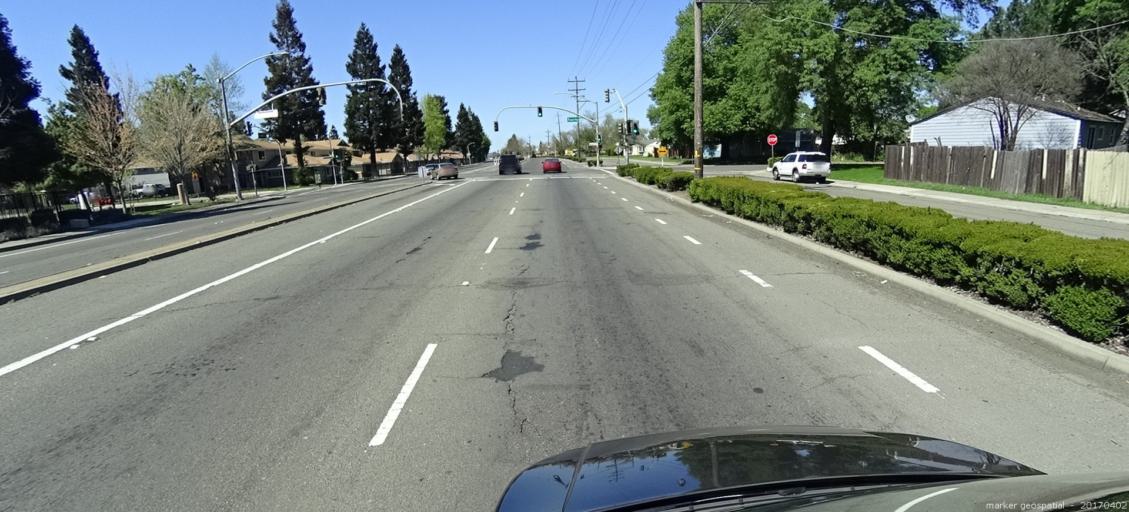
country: US
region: California
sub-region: Sacramento County
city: Parkway
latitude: 38.4870
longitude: -121.4547
